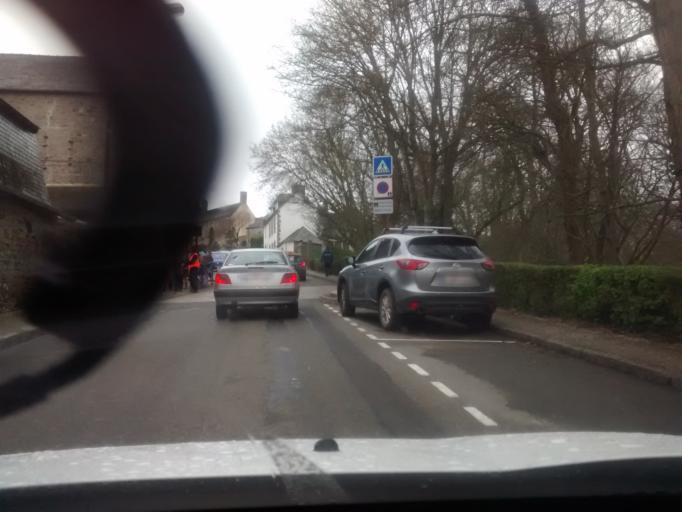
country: FR
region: Brittany
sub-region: Departement des Cotes-d'Armor
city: Treguier
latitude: 48.7897
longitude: -3.2308
